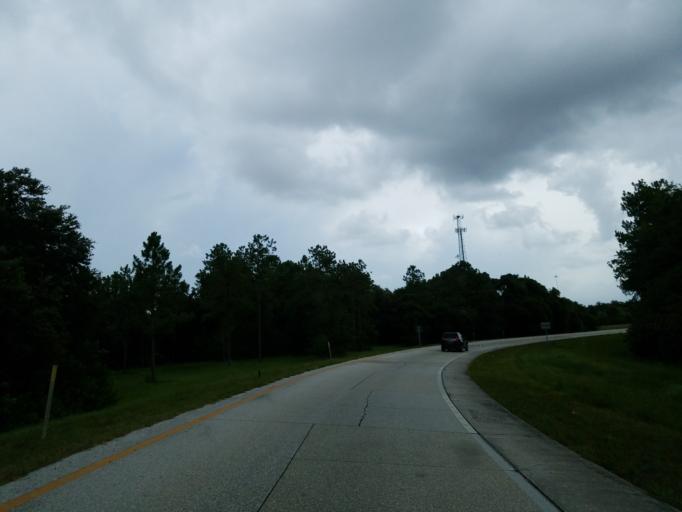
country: US
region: Florida
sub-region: Hillsborough County
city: Progress Village
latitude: 27.9046
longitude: -82.3464
